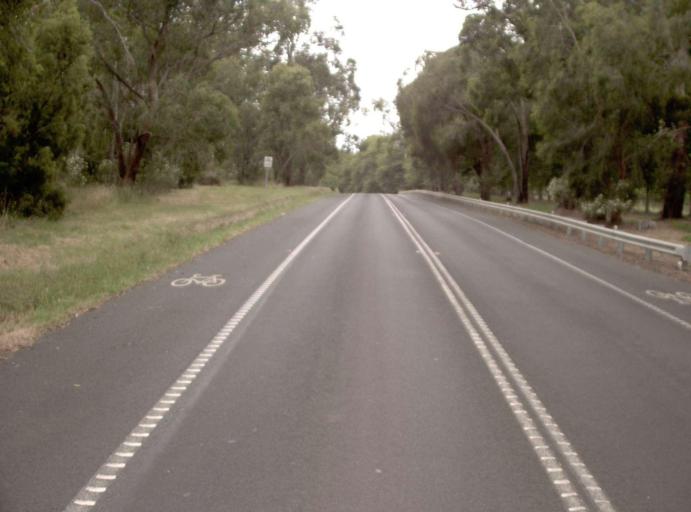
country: AU
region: Victoria
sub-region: Yarra Ranges
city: Healesville
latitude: -37.6760
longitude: 145.5066
